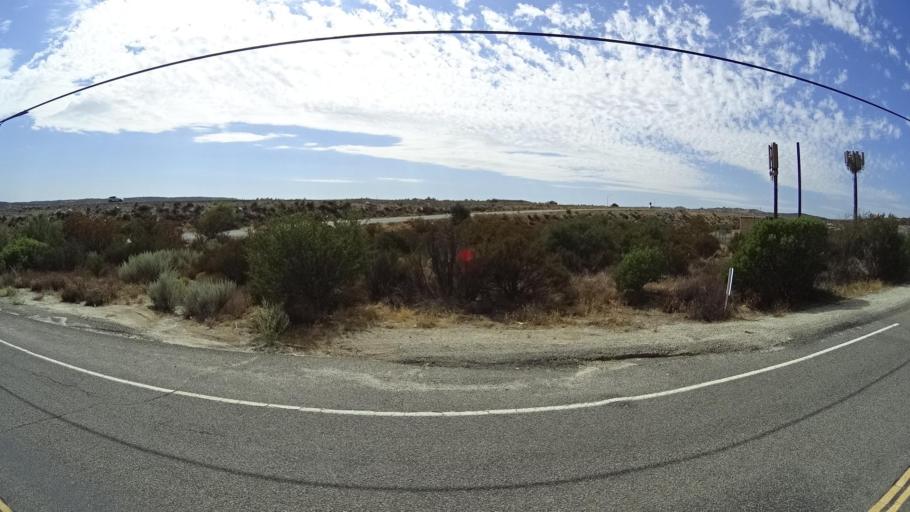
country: US
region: California
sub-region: San Diego County
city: Campo
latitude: 32.6787
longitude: -116.2918
